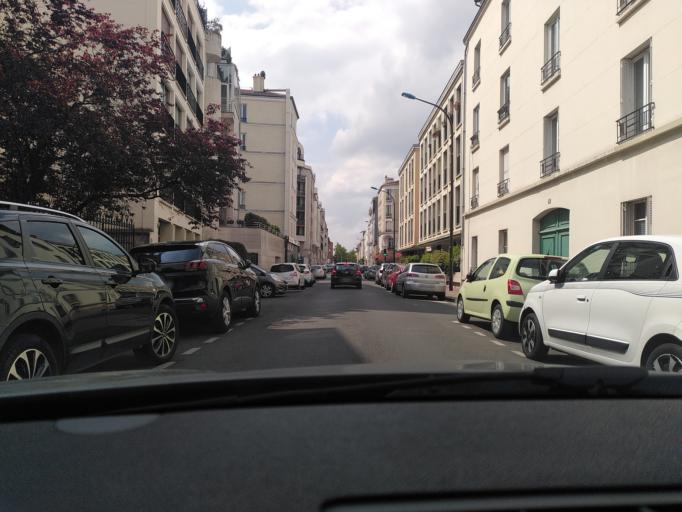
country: FR
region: Ile-de-France
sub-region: Departement du Val-de-Marne
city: Charenton-le-Pont
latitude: 48.8282
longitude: 2.4049
